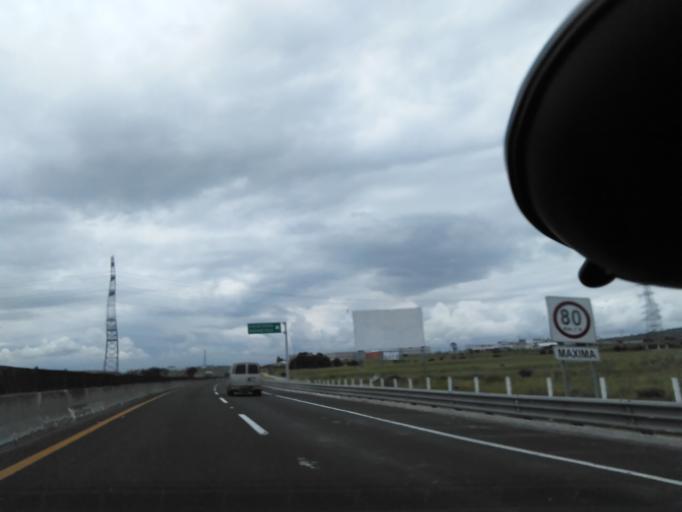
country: MX
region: Mexico
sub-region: Huehuetoca
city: Casa Nueva
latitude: 19.8236
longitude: -99.2264
